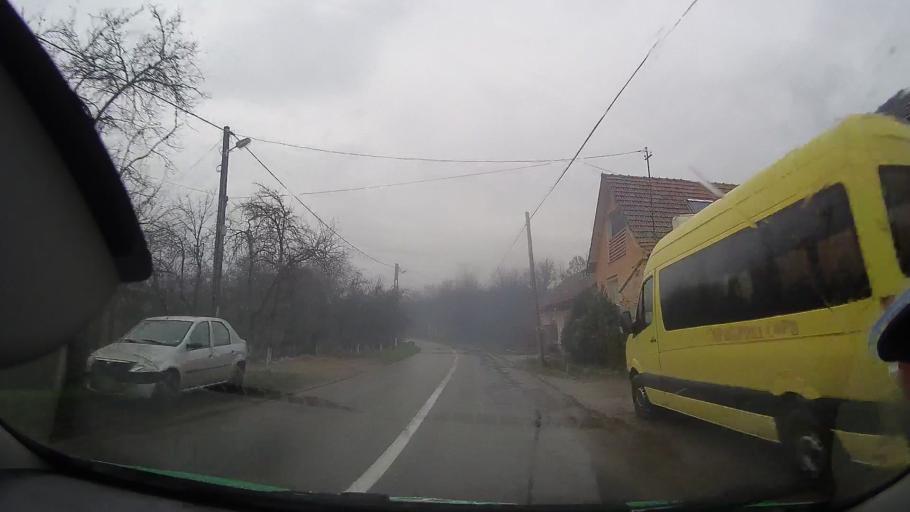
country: RO
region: Bihor
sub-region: Comuna Holod
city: Vintere
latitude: 46.7714
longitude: 22.1377
